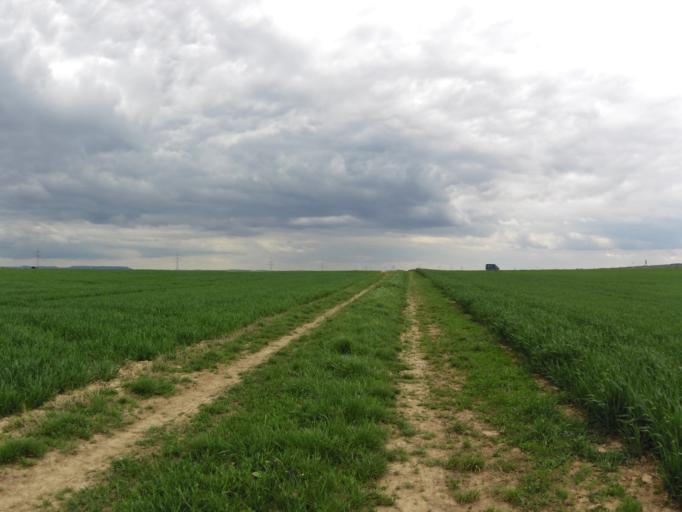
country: DE
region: Bavaria
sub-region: Regierungsbezirk Unterfranken
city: Oberpleichfeld
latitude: 49.8540
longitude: 10.0805
